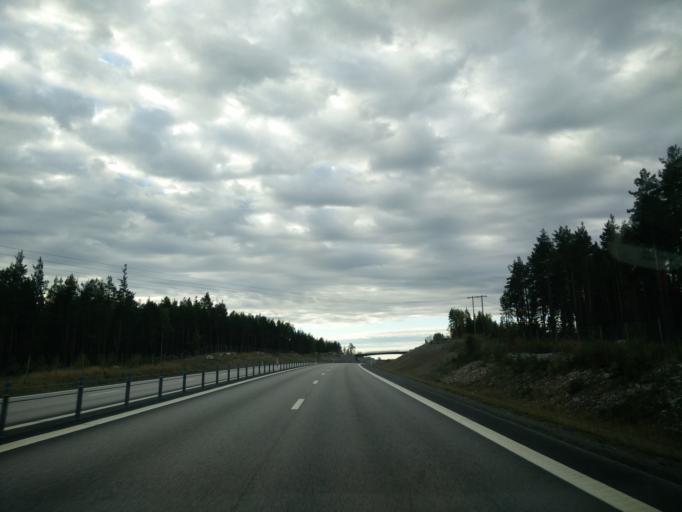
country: SE
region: Gaevleborg
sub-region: Hudiksvalls Kommun
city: Hudiksvall
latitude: 61.6966
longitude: 17.0568
